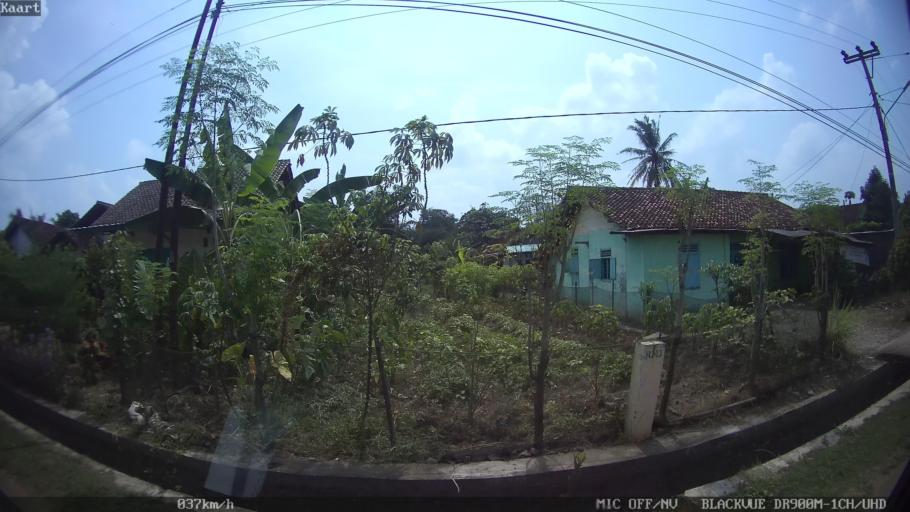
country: ID
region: Lampung
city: Pringsewu
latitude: -5.3808
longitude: 104.9685
